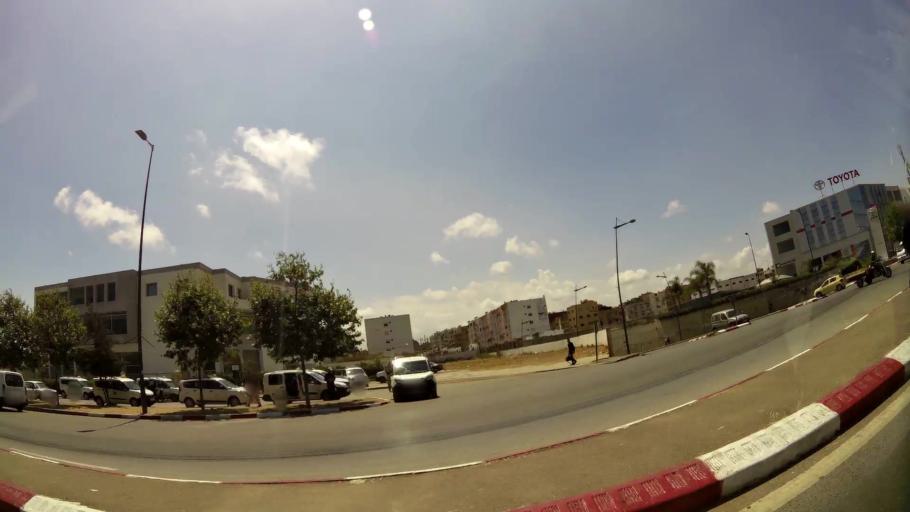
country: MA
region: Rabat-Sale-Zemmour-Zaer
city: Sale
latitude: 34.0690
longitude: -6.7912
